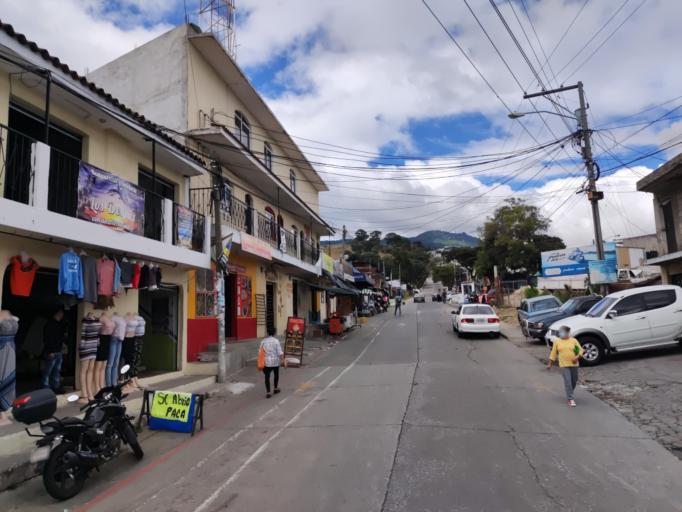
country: GT
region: Guatemala
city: Mixco
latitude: 14.5870
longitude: -90.6081
